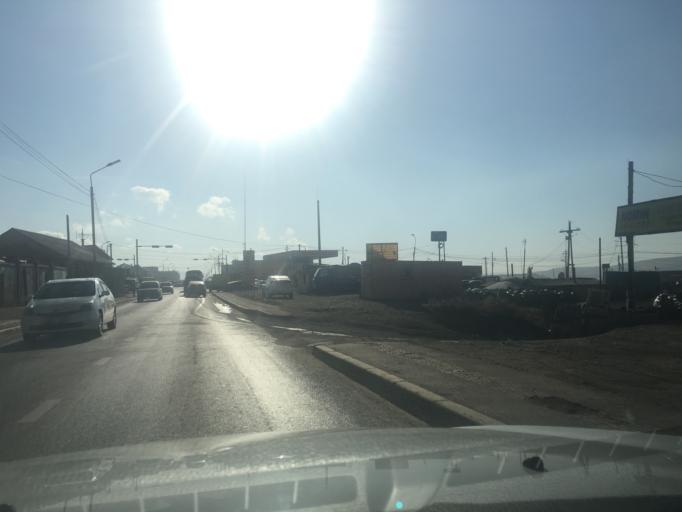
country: MN
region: Ulaanbaatar
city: Ulaanbaatar
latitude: 47.9576
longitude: 106.8265
